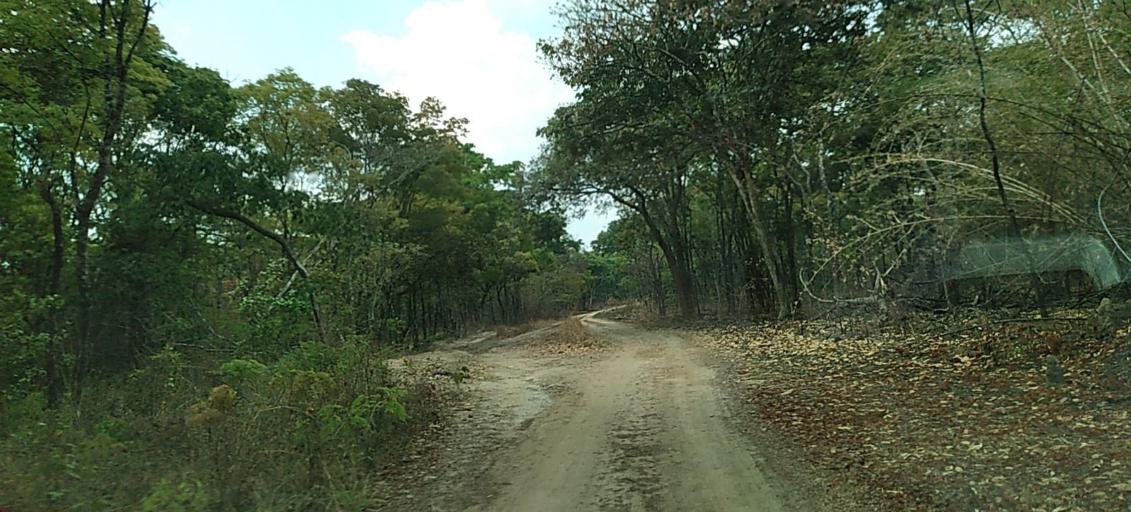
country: ZM
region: Copperbelt
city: Chingola
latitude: -12.7588
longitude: 27.7067
